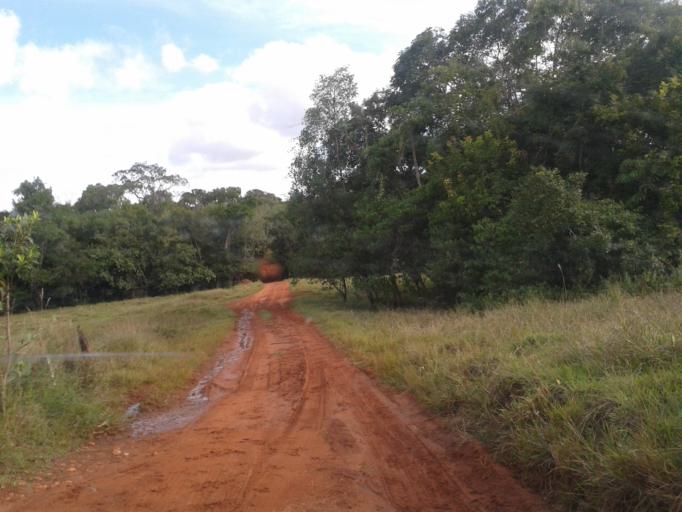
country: BR
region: Minas Gerais
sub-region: Campina Verde
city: Campina Verde
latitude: -19.4399
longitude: -49.7305
